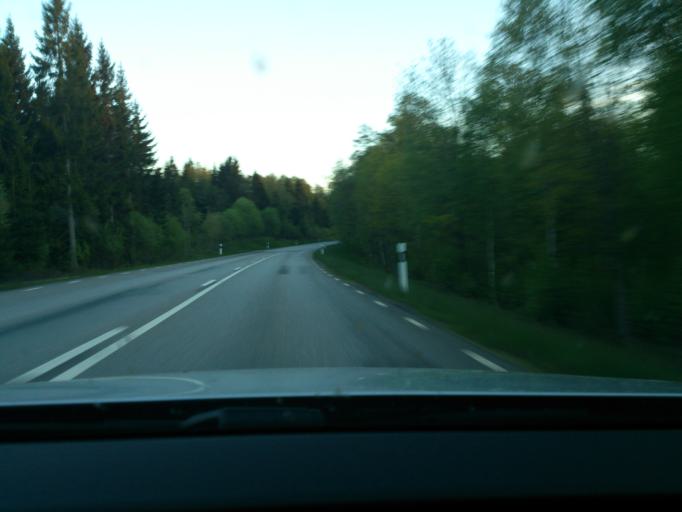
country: SE
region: Kronoberg
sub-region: Alvesta Kommun
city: Moheda
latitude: 57.0719
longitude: 14.6112
